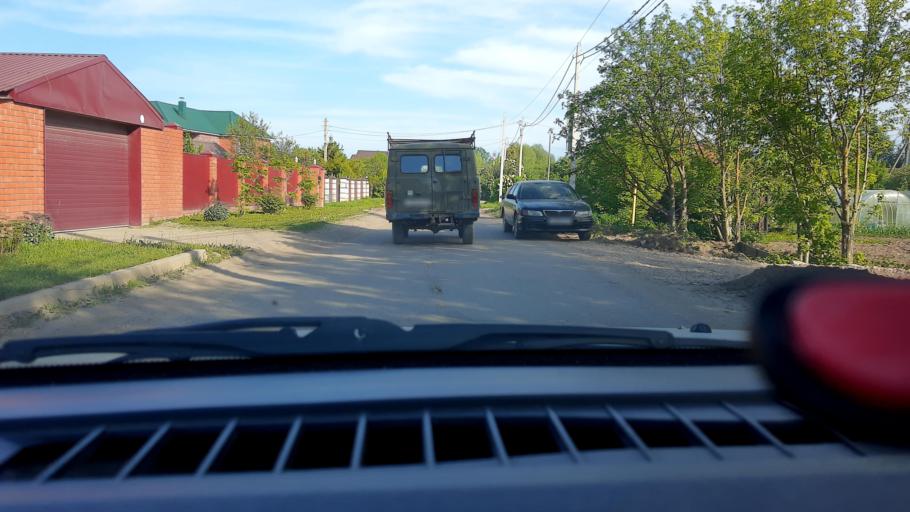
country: RU
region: Nizjnij Novgorod
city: Afonino
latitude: 56.2455
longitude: 44.0818
